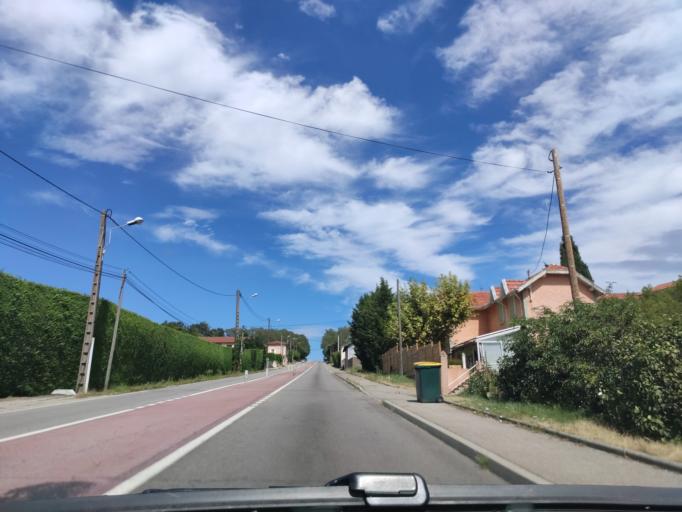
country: FR
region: Rhone-Alpes
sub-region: Departement de l'Isere
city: Roussillon
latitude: 45.3859
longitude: 4.8017
